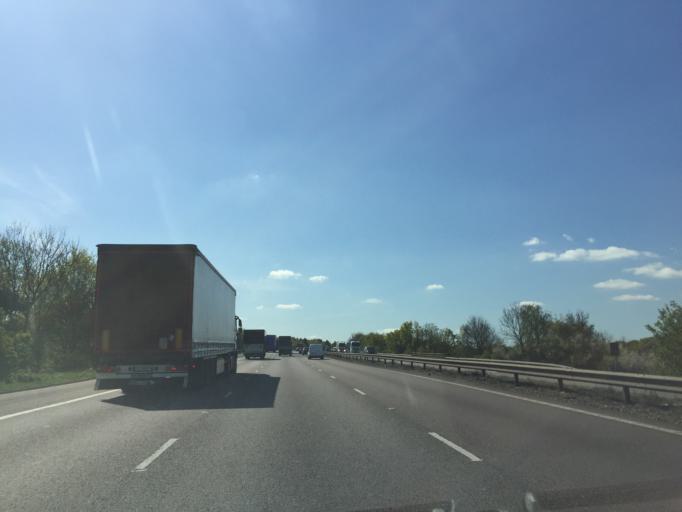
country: GB
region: England
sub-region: Essex
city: Epping
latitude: 51.7137
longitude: 0.1448
